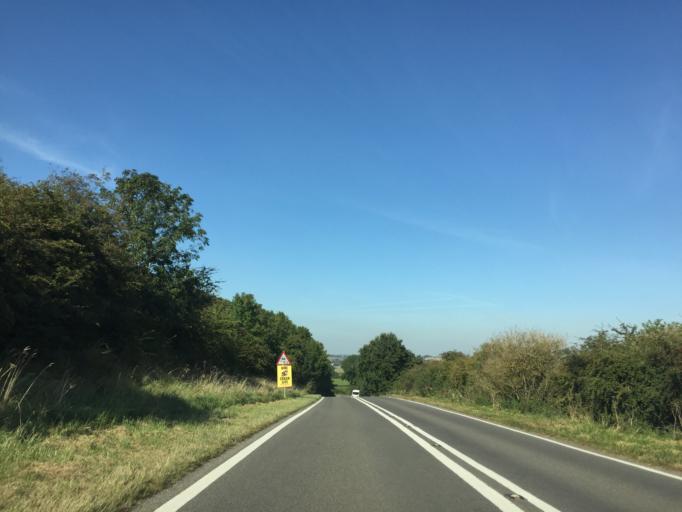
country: GB
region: England
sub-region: Leicestershire
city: Houghton on the Hill
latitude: 52.6518
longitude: -0.9082
